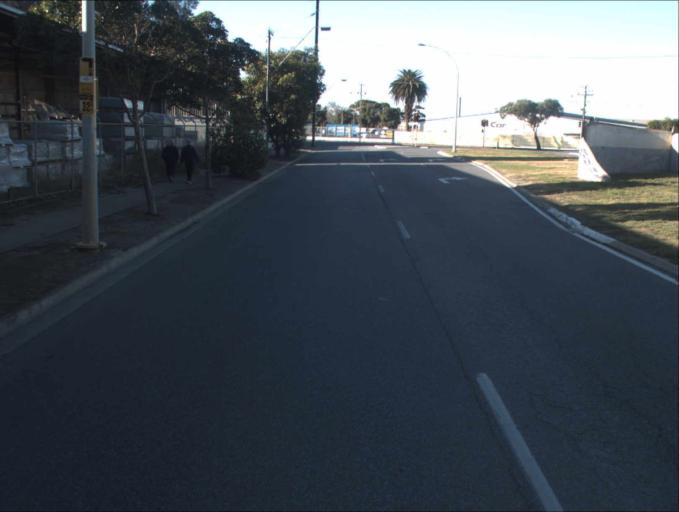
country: AU
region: South Australia
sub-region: Port Adelaide Enfield
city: Alberton
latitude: -34.8501
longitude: 138.5364
